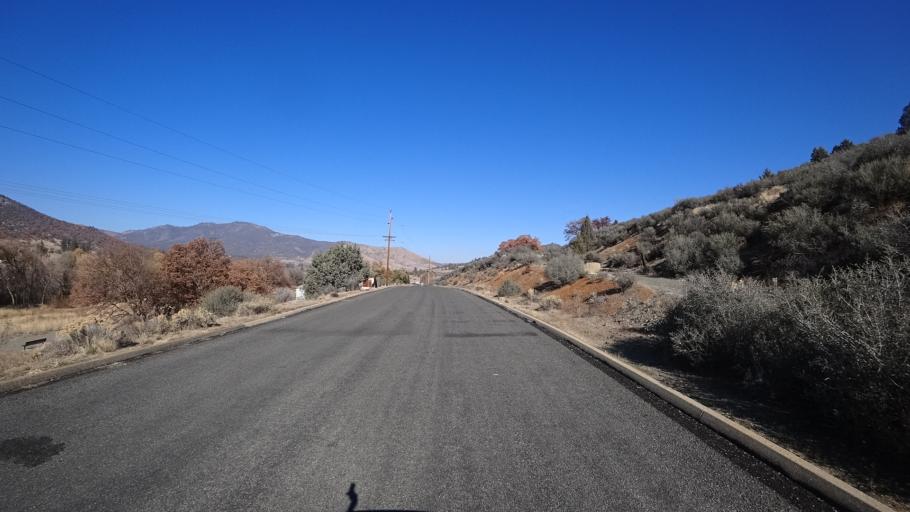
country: US
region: California
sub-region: Siskiyou County
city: Yreka
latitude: 41.7425
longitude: -122.6283
